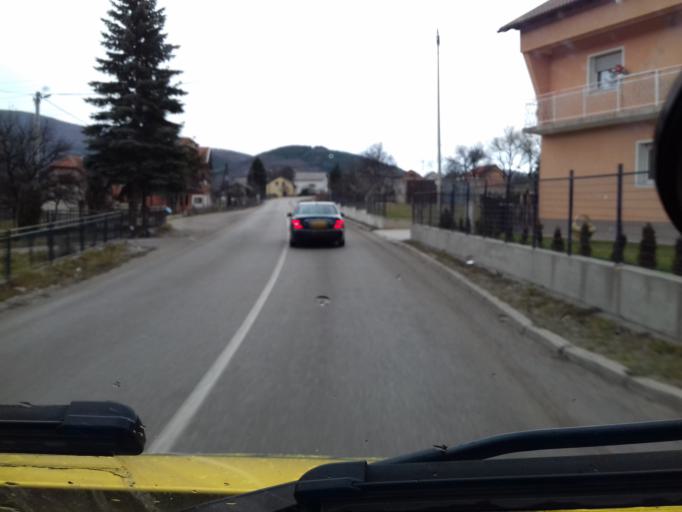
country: BA
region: Federation of Bosnia and Herzegovina
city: Turbe
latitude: 44.2464
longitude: 17.5729
